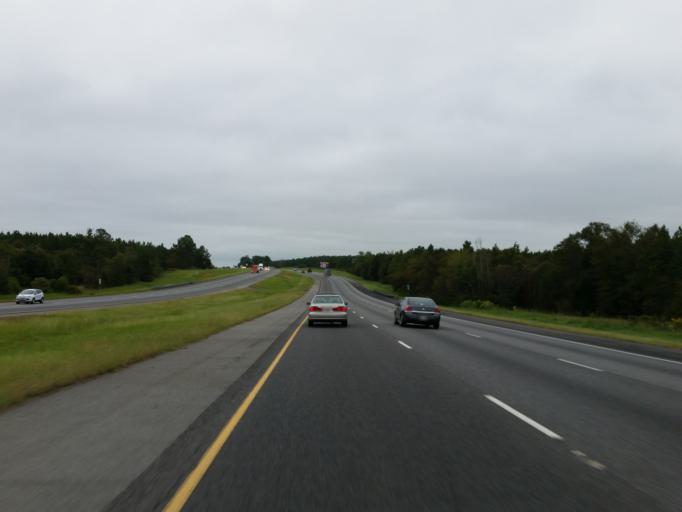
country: US
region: Georgia
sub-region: Turner County
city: Ashburn
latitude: 31.8133
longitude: -83.7083
